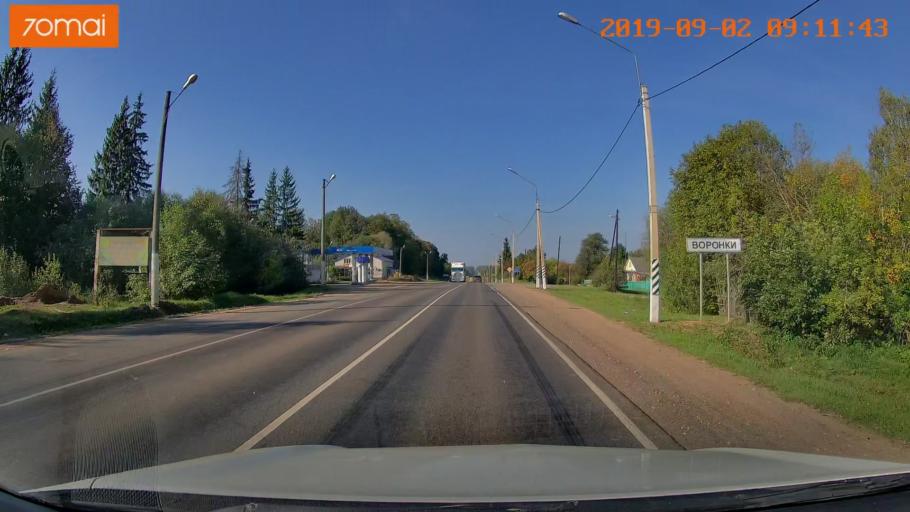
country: RU
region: Kaluga
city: Myatlevo
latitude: 54.8653
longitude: 35.5695
